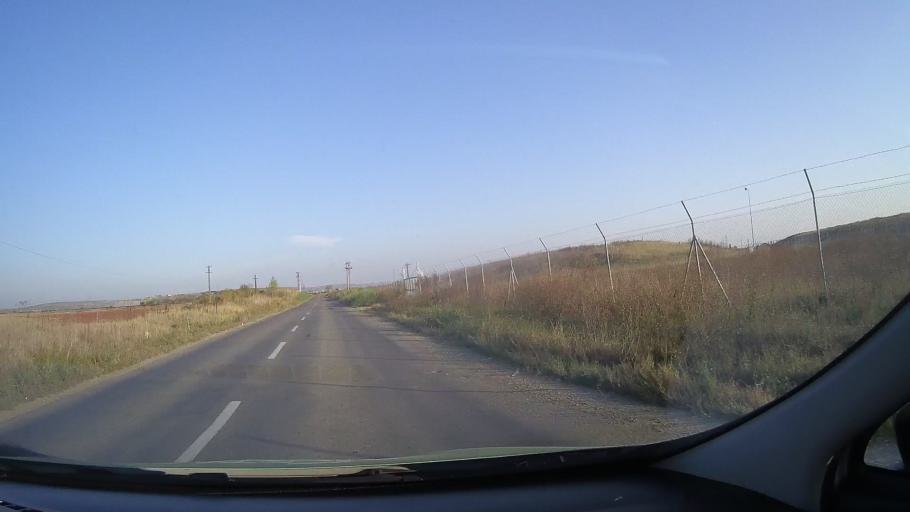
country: RO
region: Bihor
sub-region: Comuna Bors
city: Santion
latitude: 47.1125
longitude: 21.8578
